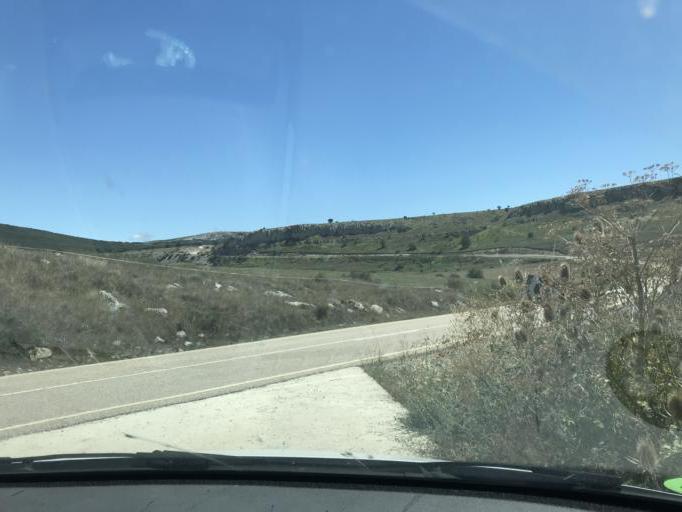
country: ES
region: Castille and Leon
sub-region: Provincia de Palencia
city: Dehesa de Montejo
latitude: 42.8241
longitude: -4.5021
